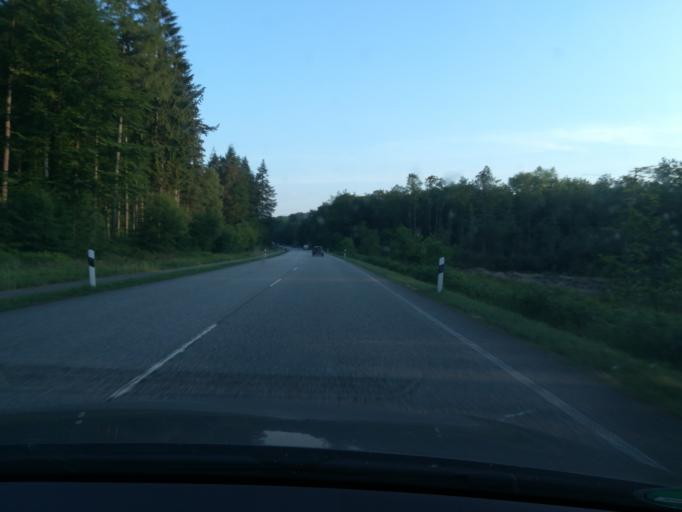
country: DE
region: Schleswig-Holstein
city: Brunstorf
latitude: 53.5220
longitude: 10.4483
